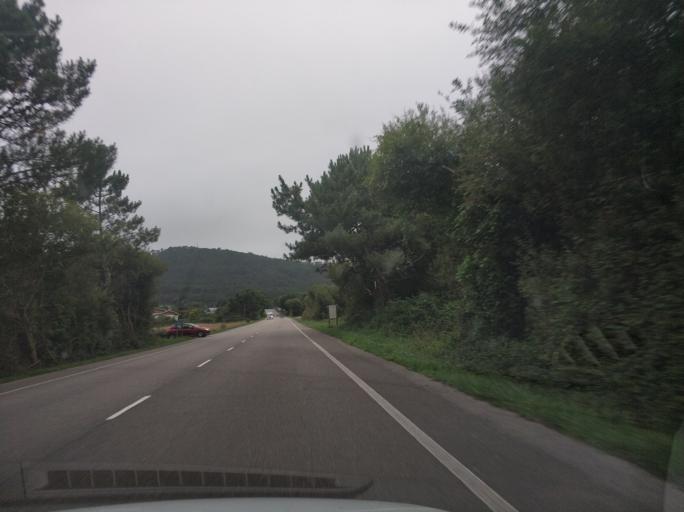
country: ES
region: Asturias
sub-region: Province of Asturias
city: Cudillero
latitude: 43.5601
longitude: -6.1643
